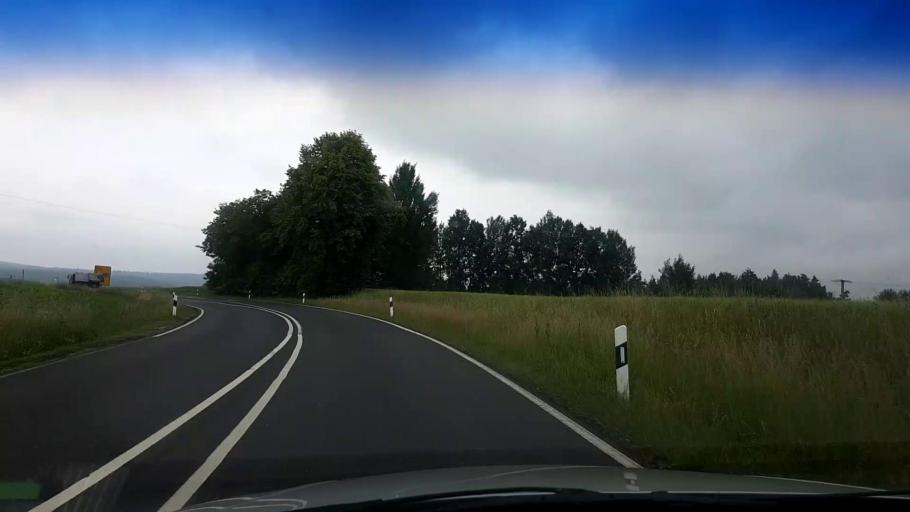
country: DE
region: Bavaria
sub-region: Upper Franconia
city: Hohenberg an der Eger
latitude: 50.0894
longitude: 12.2176
